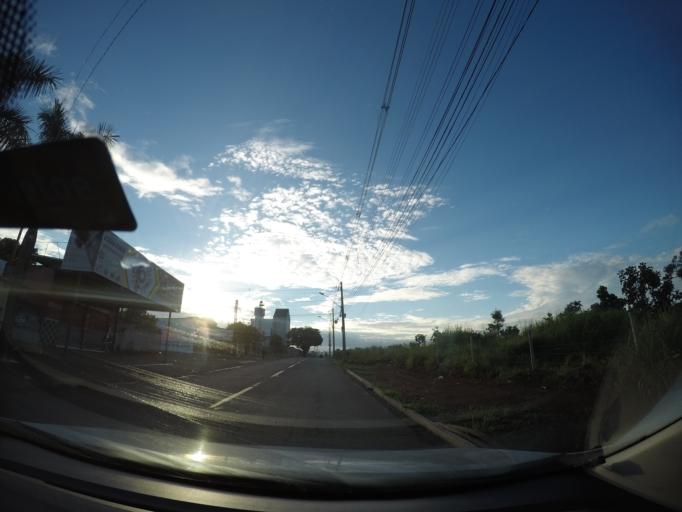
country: BR
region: Goias
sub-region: Goiania
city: Goiania
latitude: -16.7018
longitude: -49.3452
